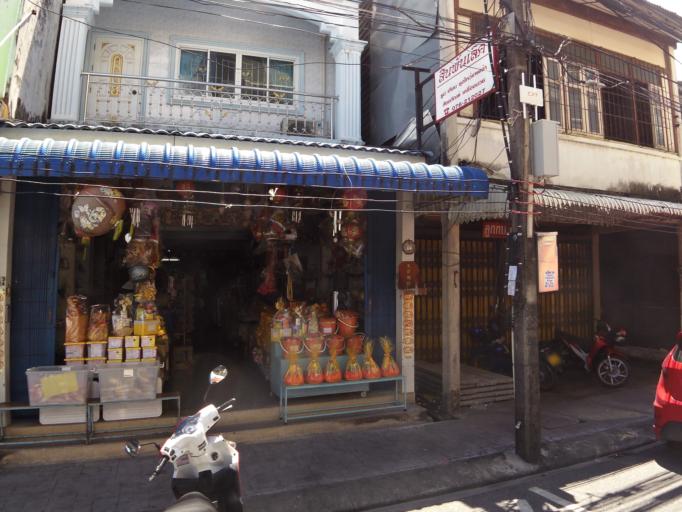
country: TH
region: Phuket
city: Ban Talat Nua
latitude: 7.8834
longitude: 98.3851
